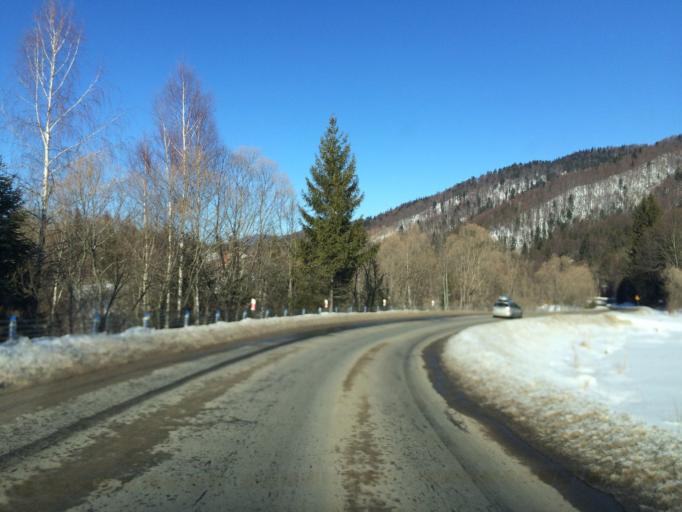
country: PL
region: Subcarpathian Voivodeship
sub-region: Powiat leski
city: Cisna
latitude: 49.1850
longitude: 22.3853
